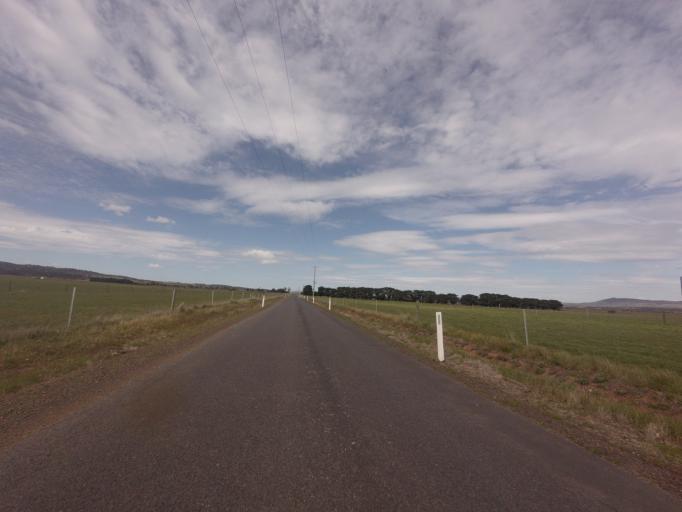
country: AU
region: Tasmania
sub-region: Northern Midlands
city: Evandale
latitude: -41.8129
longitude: 147.2918
